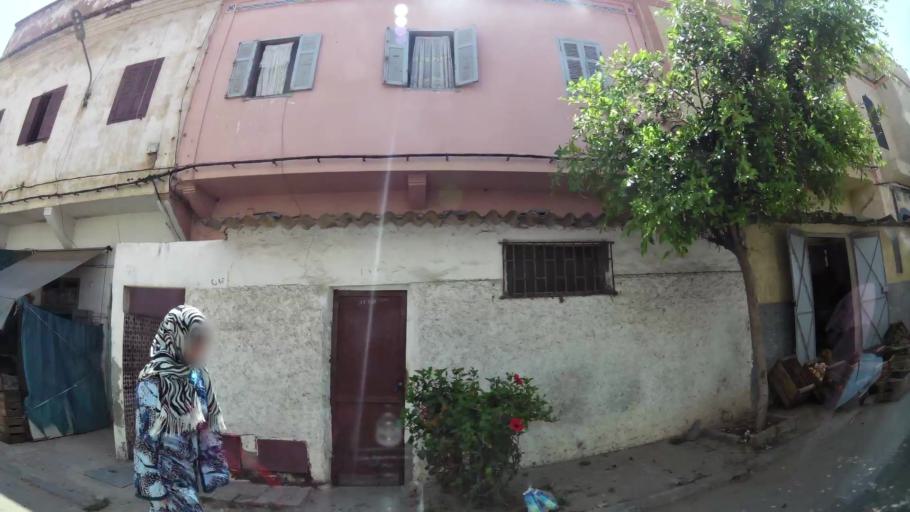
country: MA
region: Rabat-Sale-Zemmour-Zaer
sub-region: Rabat
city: Rabat
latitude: 34.0112
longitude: -6.8610
